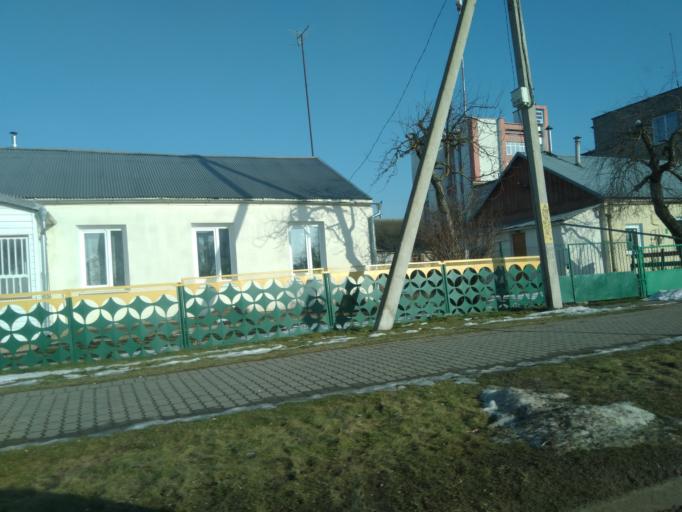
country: BY
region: Minsk
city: Snow
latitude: 53.2223
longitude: 26.3994
